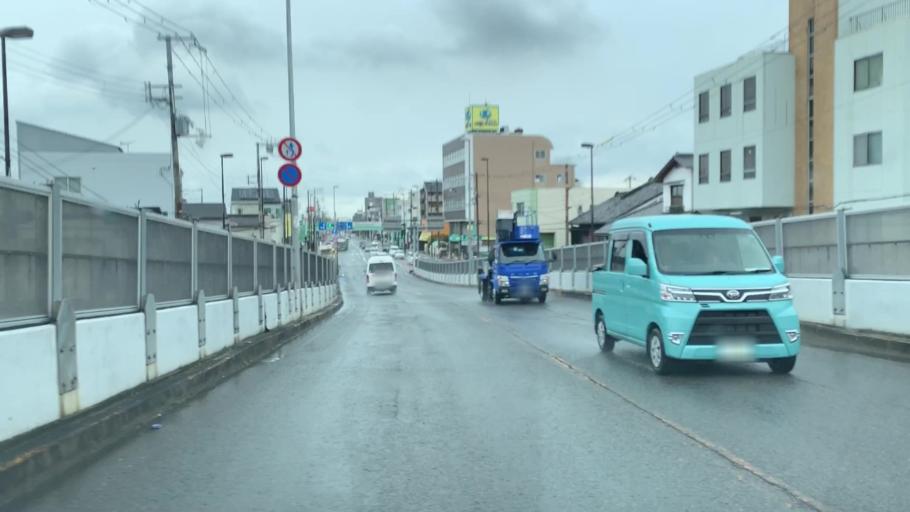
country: JP
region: Wakayama
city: Wakayama-shi
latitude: 34.2291
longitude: 135.1612
